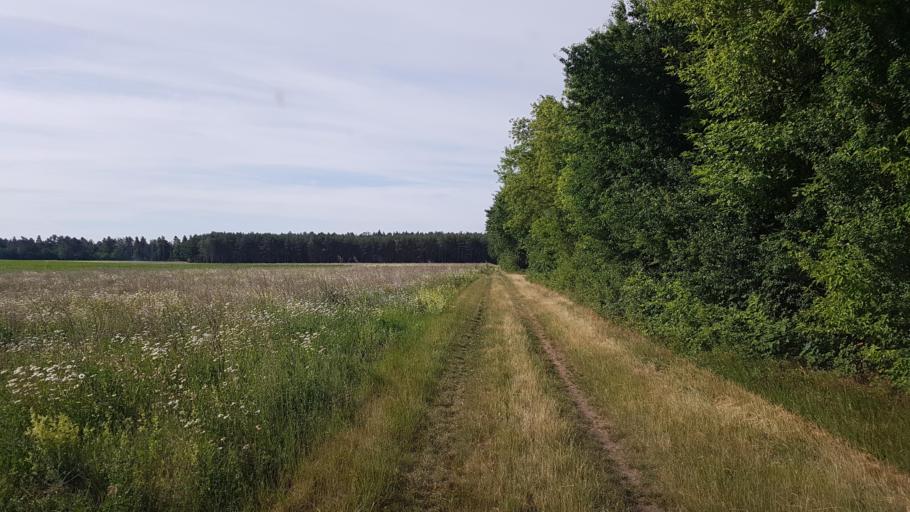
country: DE
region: Brandenburg
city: Plessa
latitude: 51.5333
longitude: 13.6499
